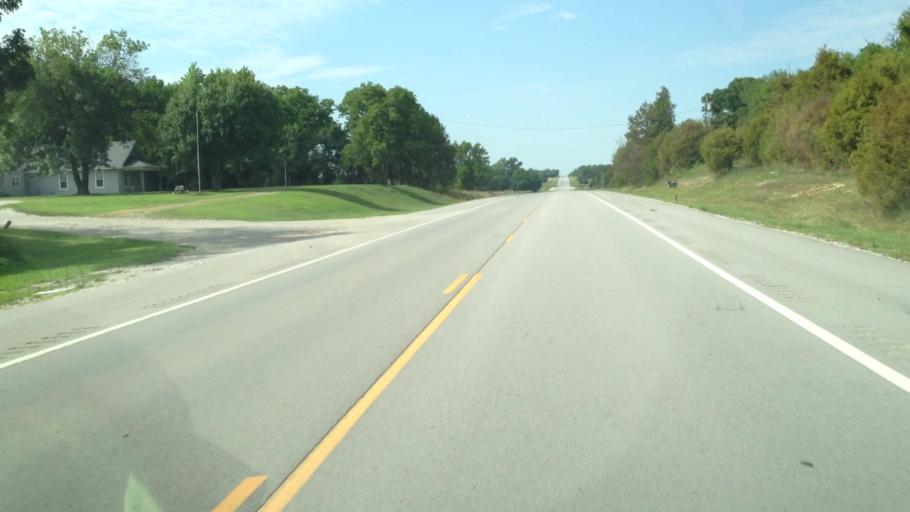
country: US
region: Kansas
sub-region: Labette County
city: Parsons
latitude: 37.2886
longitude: -95.2675
